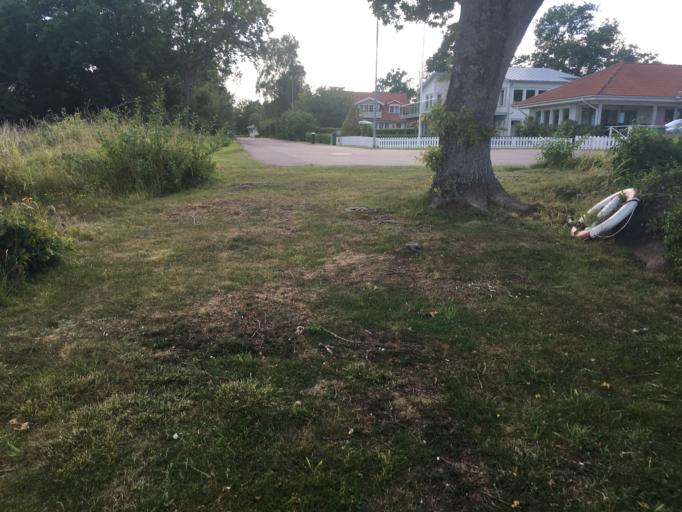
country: SE
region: Kalmar
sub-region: Kalmar Kommun
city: Kalmar
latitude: 56.7009
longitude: 16.3740
